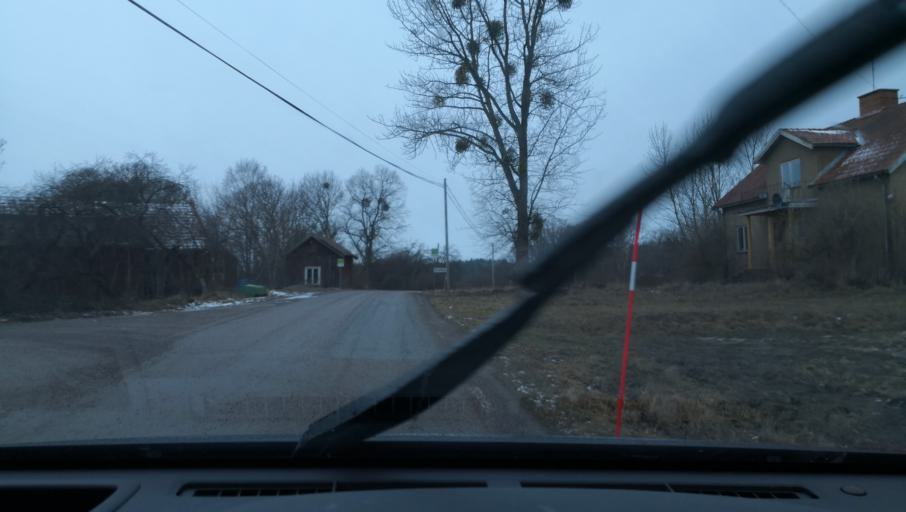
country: SE
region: Soedermanland
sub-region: Strangnas Kommun
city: Strangnas
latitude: 59.4523
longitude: 16.8618
